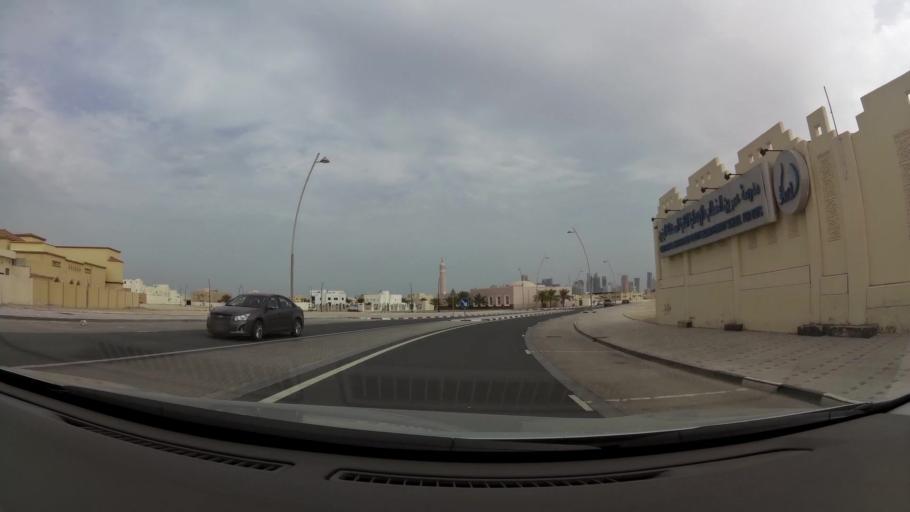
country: QA
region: Baladiyat ad Dawhah
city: Doha
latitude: 25.3460
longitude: 51.4978
